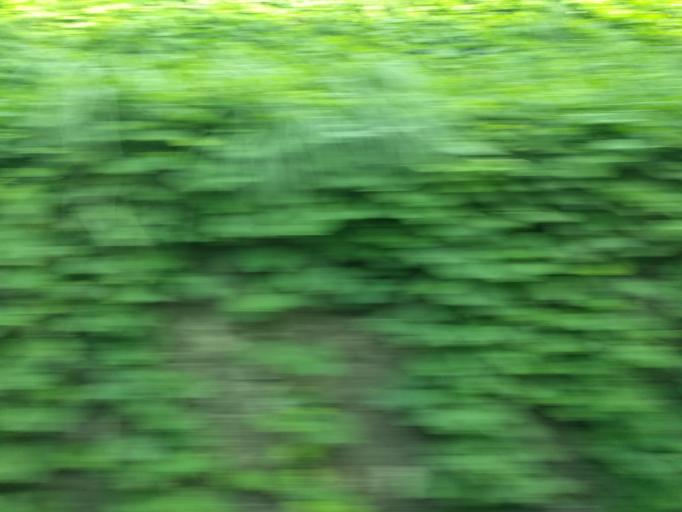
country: JP
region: Kanagawa
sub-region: Kawasaki-shi
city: Kawasaki
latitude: 35.5988
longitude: 139.6882
